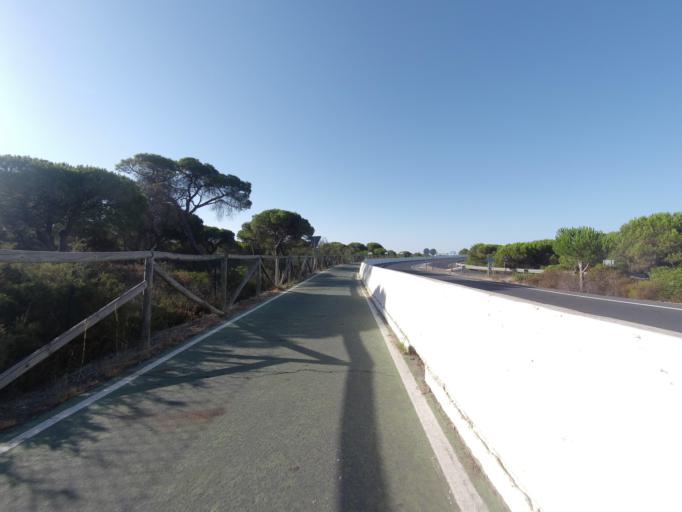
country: ES
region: Andalusia
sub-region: Provincia de Huelva
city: Aljaraque
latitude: 37.2270
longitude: -7.0217
